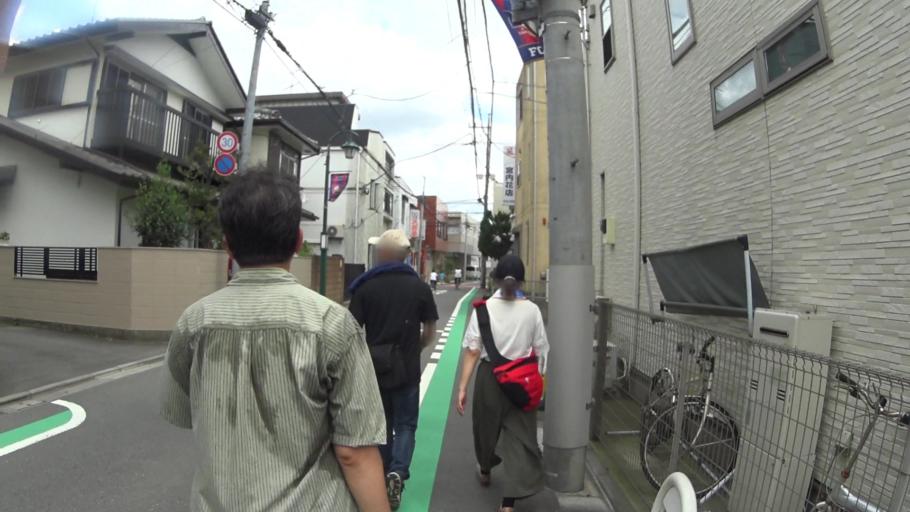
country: JP
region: Tokyo
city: Chofugaoka
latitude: 35.6572
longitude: 139.5649
